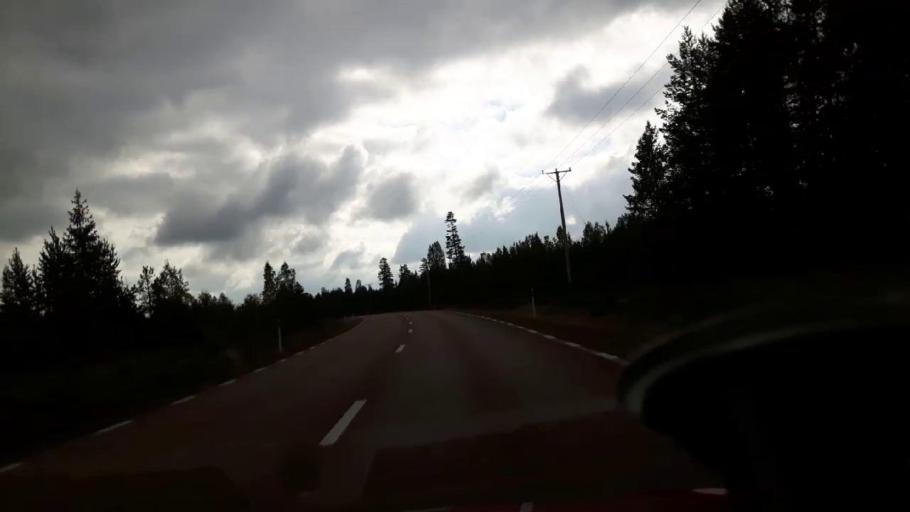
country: SE
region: Gaevleborg
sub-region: Soderhamns Kommun
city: Ljusne
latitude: 61.1141
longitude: 16.9348
